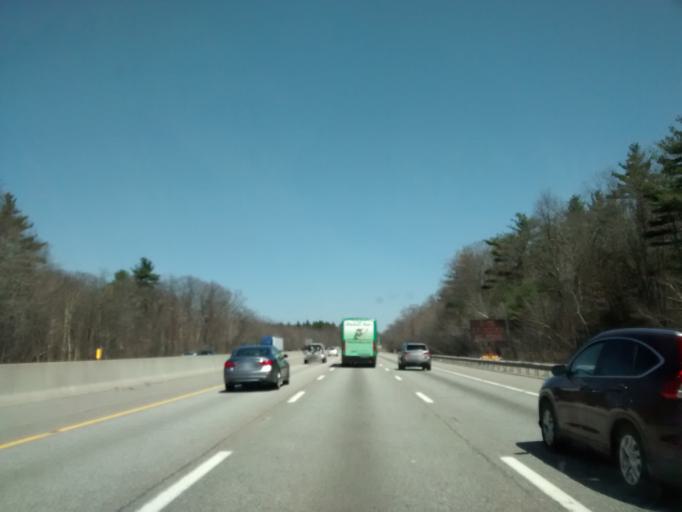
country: US
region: Massachusetts
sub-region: Worcester County
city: Westborough
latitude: 42.2566
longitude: -71.5800
